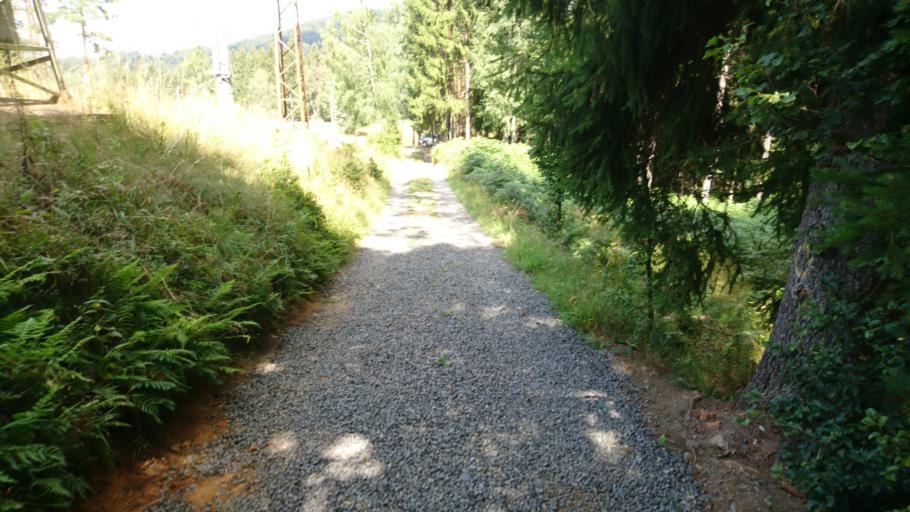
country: CZ
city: Novy Bor
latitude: 50.8130
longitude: 14.5428
